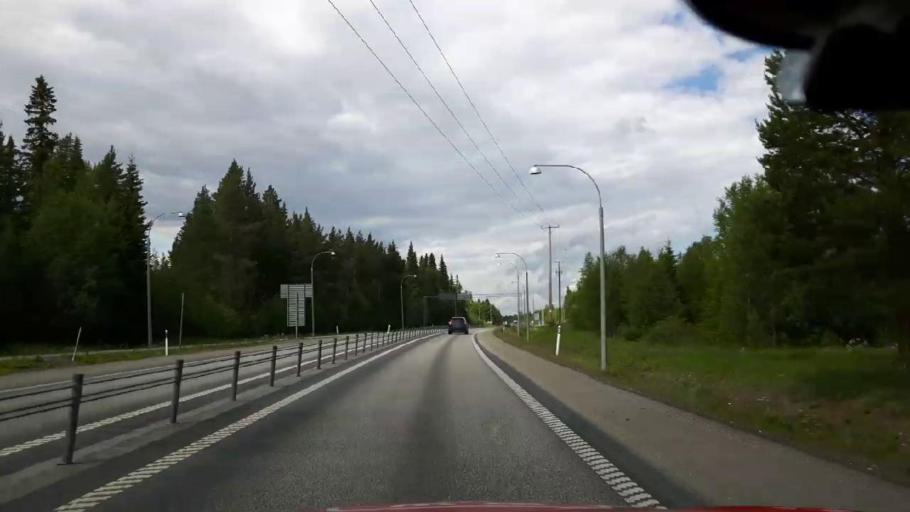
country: SE
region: Jaemtland
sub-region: OEstersunds Kommun
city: Ostersund
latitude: 63.2183
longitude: 14.6310
